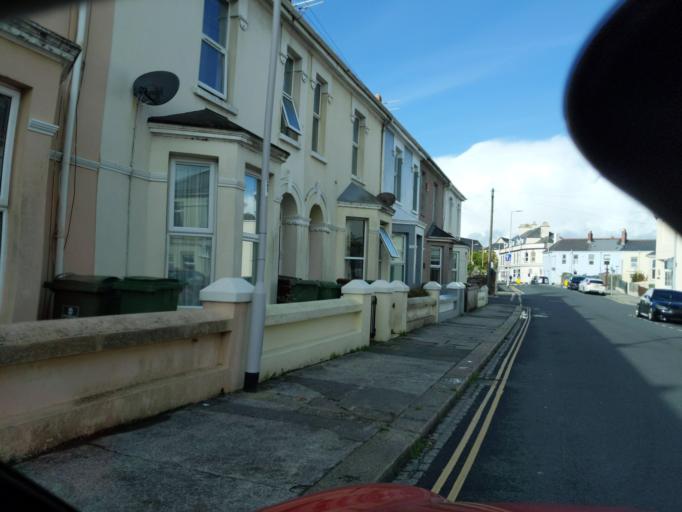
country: GB
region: England
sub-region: Plymouth
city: Plymouth
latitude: 50.3678
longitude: -4.1216
